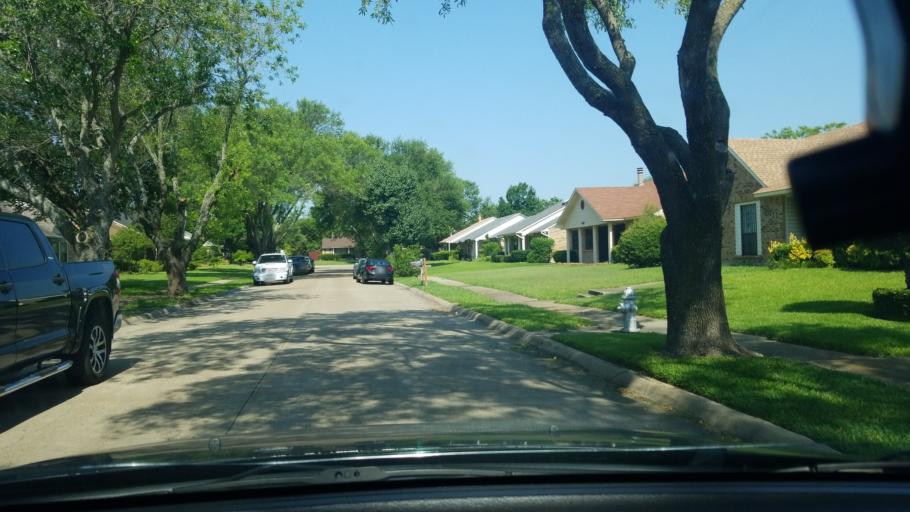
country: US
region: Texas
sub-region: Dallas County
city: Mesquite
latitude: 32.8211
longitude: -96.6222
